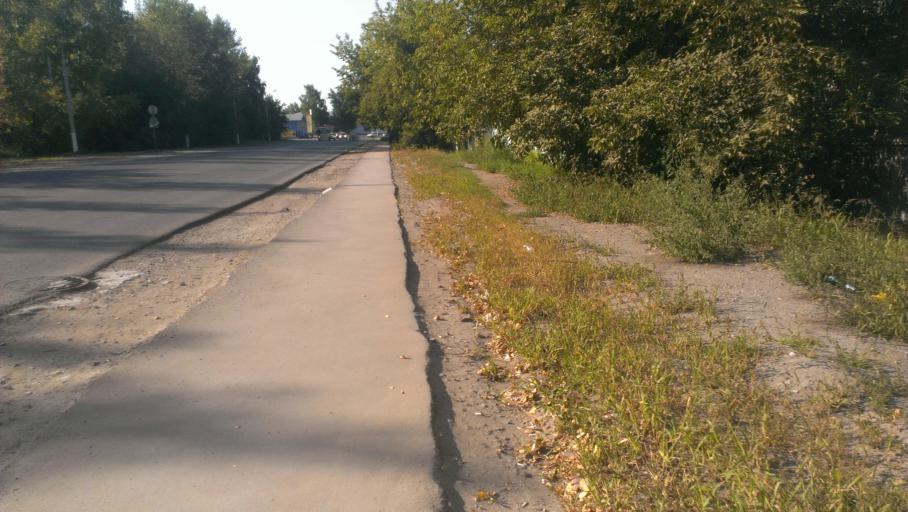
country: RU
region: Altai Krai
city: Novosilikatnyy
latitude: 53.3096
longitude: 83.6221
